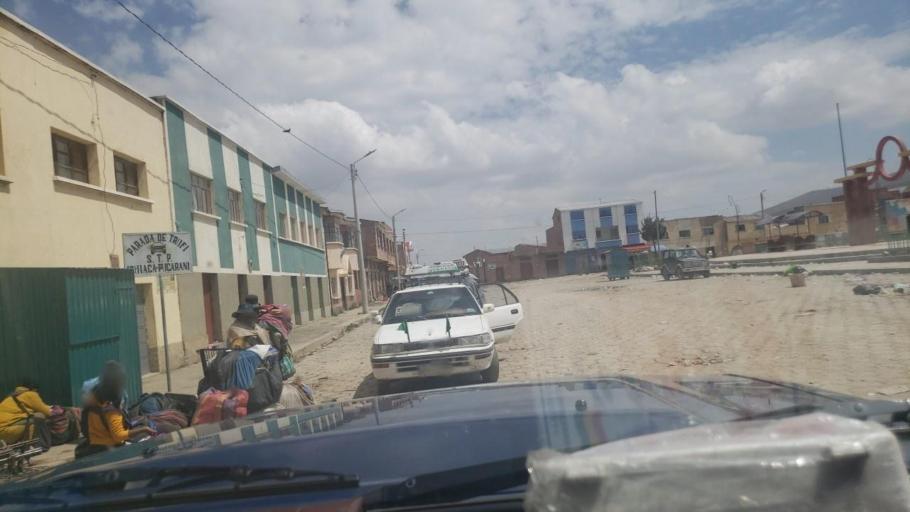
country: BO
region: La Paz
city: Batallas
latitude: -16.4086
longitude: -68.5410
